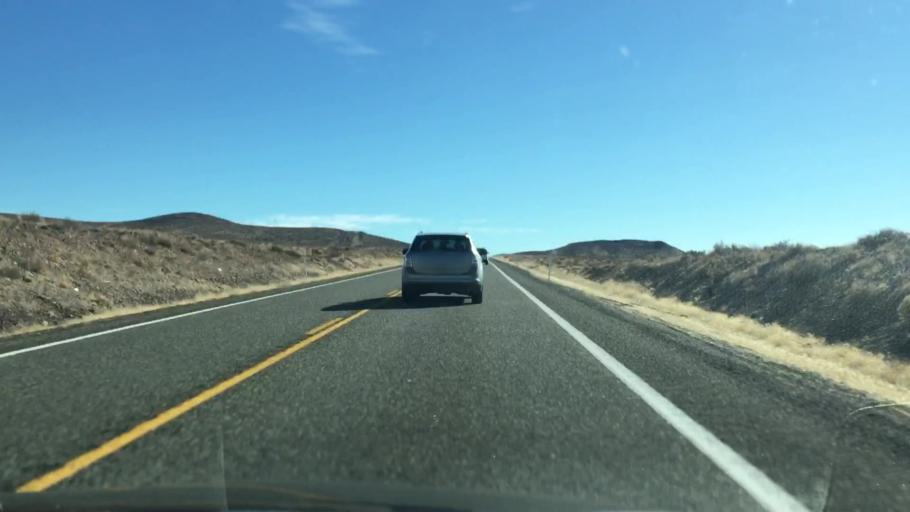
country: US
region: Nevada
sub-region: Lyon County
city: Silver Springs
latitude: 39.2334
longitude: -119.2318
